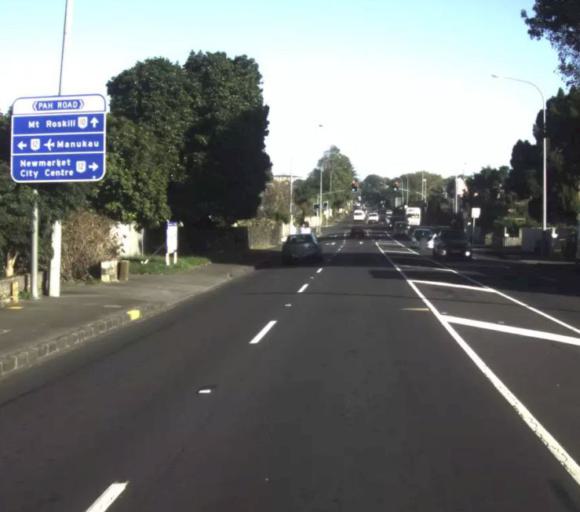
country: NZ
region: Auckland
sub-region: Auckland
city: Auckland
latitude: -36.9110
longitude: 174.7711
